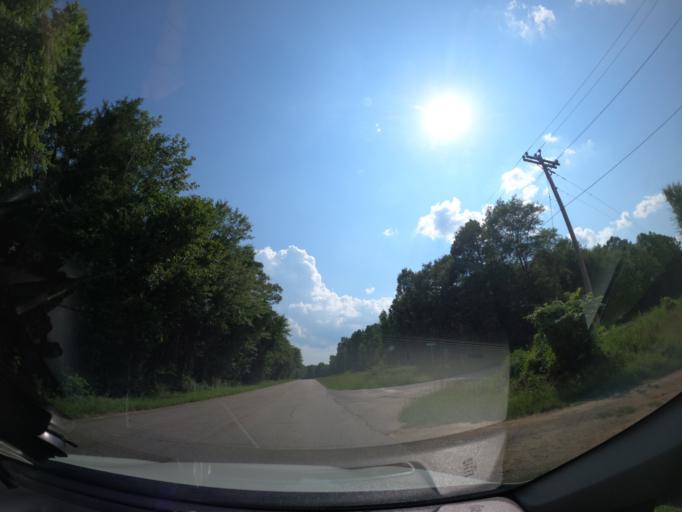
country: US
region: South Carolina
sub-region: Barnwell County
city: Williston
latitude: 33.5843
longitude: -81.4724
